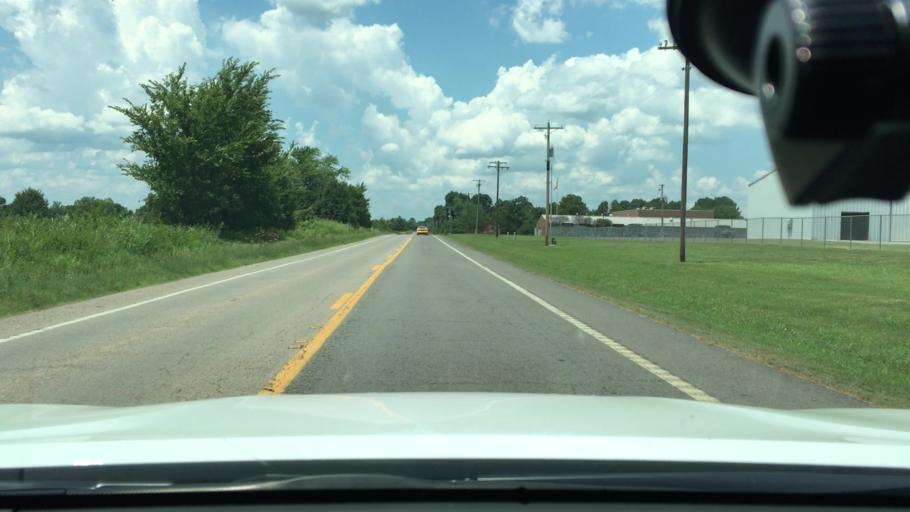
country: US
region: Arkansas
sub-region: Logan County
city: Booneville
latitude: 35.1478
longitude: -93.8663
